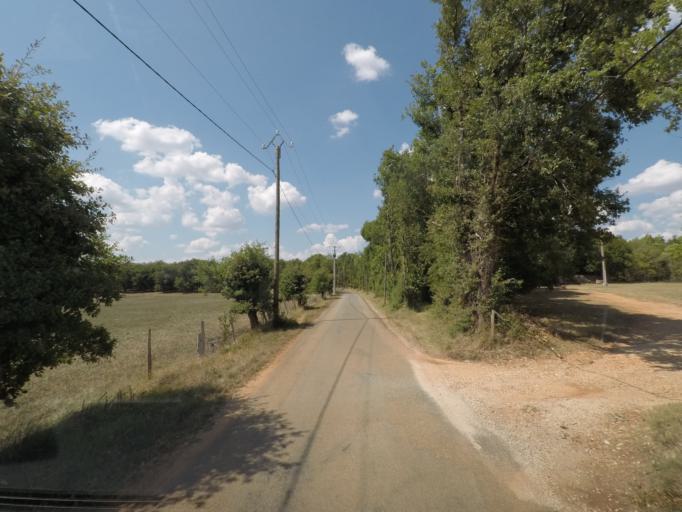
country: FR
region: Midi-Pyrenees
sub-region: Departement du Lot
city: Cahors
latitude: 44.5329
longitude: 1.6128
